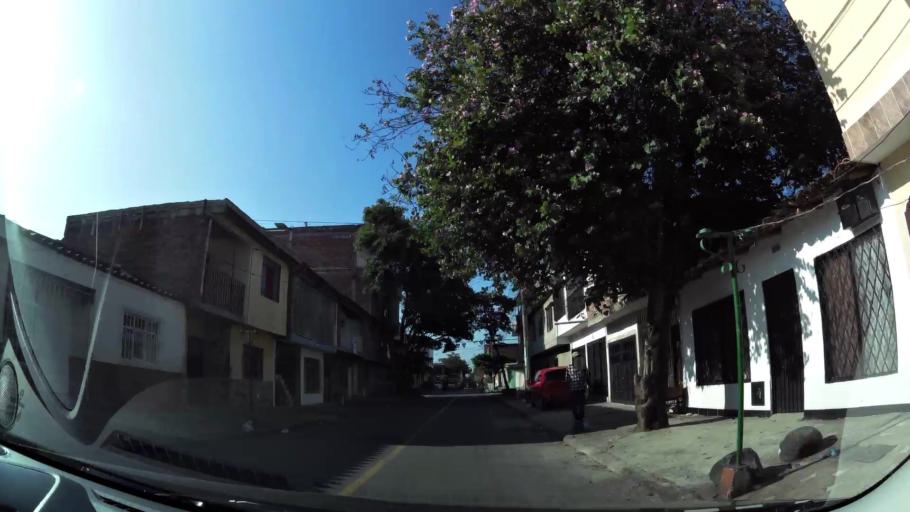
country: CO
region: Valle del Cauca
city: Cali
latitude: 3.4265
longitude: -76.5096
